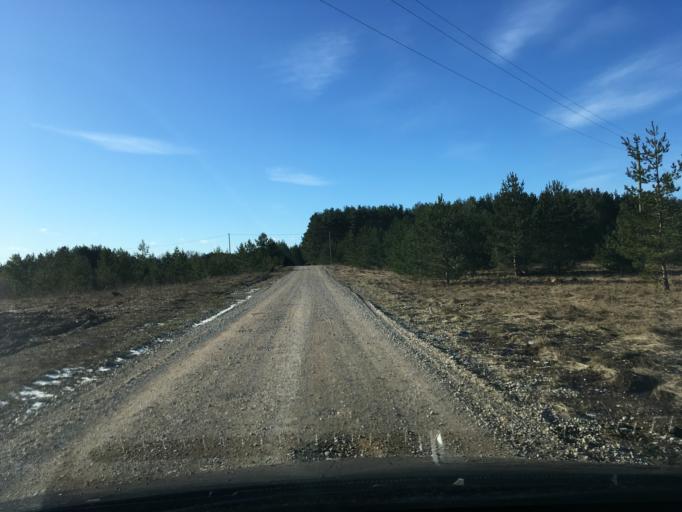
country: EE
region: Laeaene
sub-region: Lihula vald
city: Lihula
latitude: 58.5818
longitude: 23.7043
